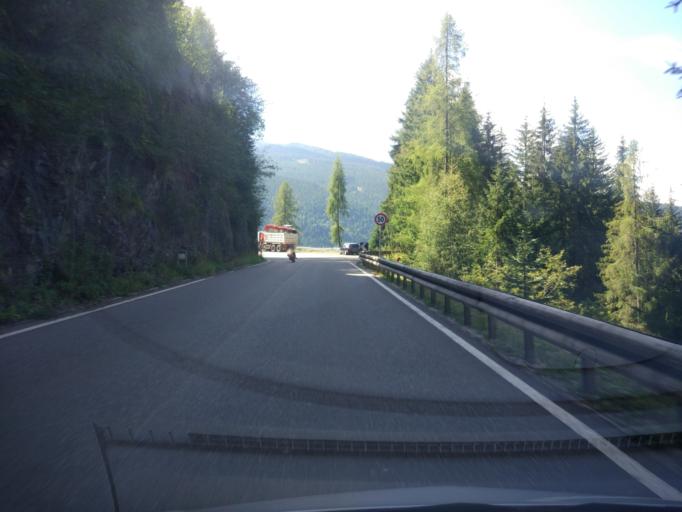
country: IT
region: Trentino-Alto Adige
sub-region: Provincia di Trento
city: Moena
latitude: 46.3121
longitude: 11.6791
